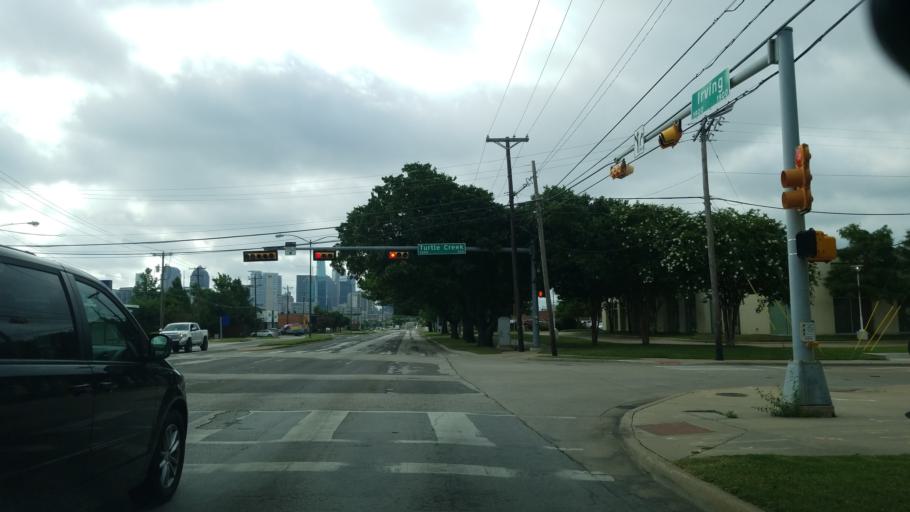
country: US
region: Texas
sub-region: Dallas County
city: Dallas
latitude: 32.7941
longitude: -96.8267
